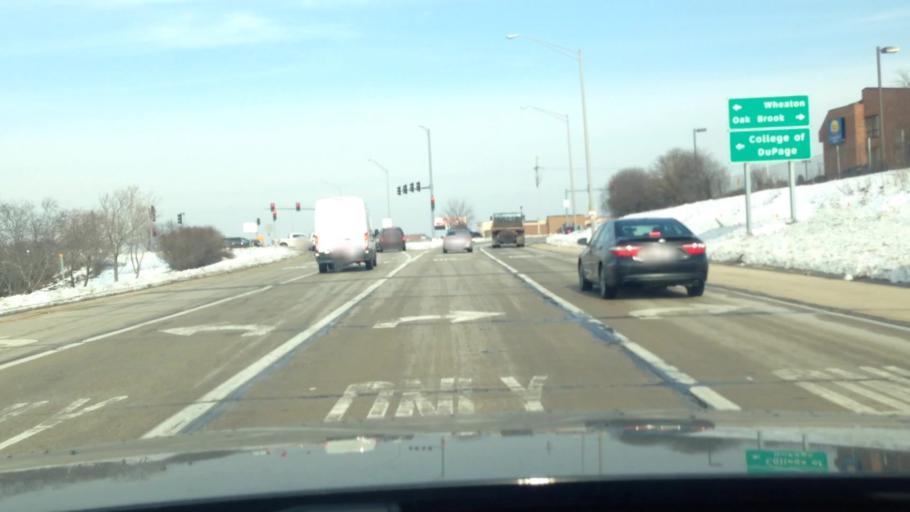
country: US
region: Illinois
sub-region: DuPage County
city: Downers Grove
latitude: 41.8320
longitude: -88.0278
